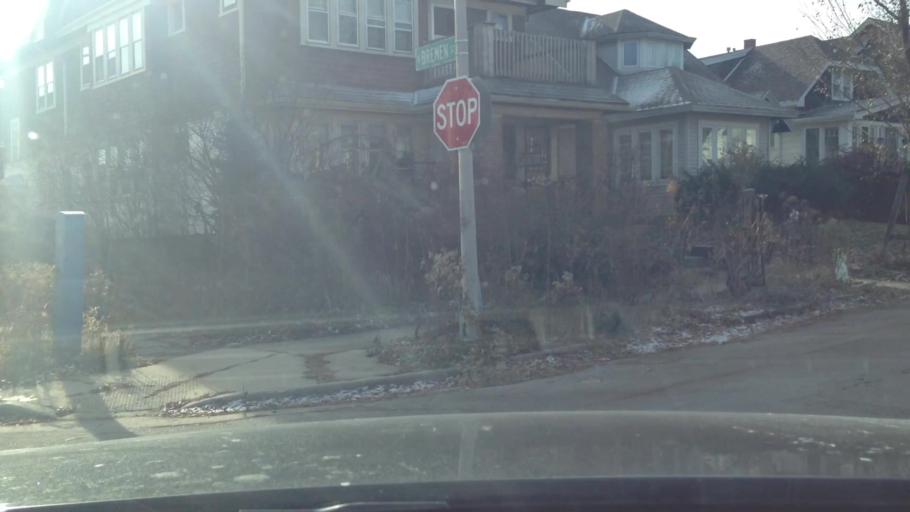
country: US
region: Wisconsin
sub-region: Milwaukee County
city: Shorewood
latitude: 43.0798
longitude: -87.9002
